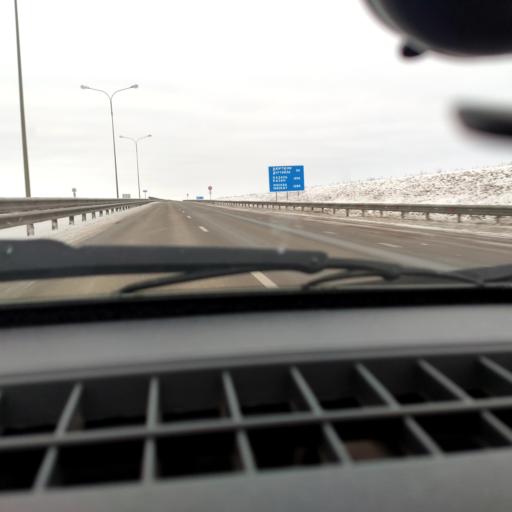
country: RU
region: Bashkortostan
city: Kushnarenkovo
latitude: 55.0816
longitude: 55.2669
